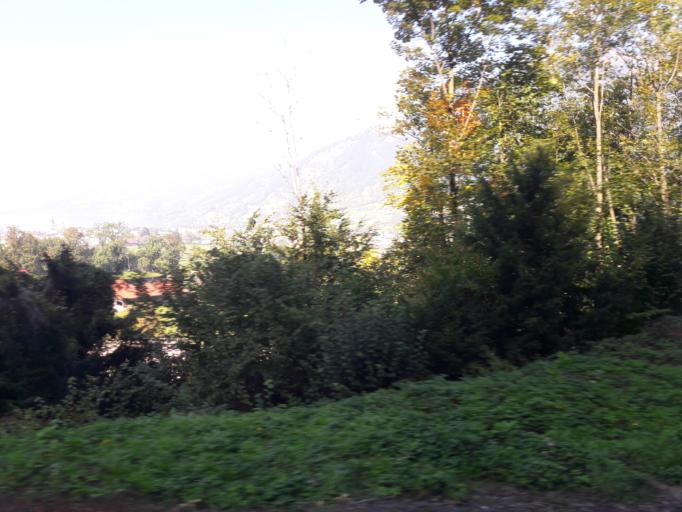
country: CH
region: Schwyz
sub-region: Bezirk Schwyz
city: Arth
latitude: 47.0508
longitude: 8.5286
